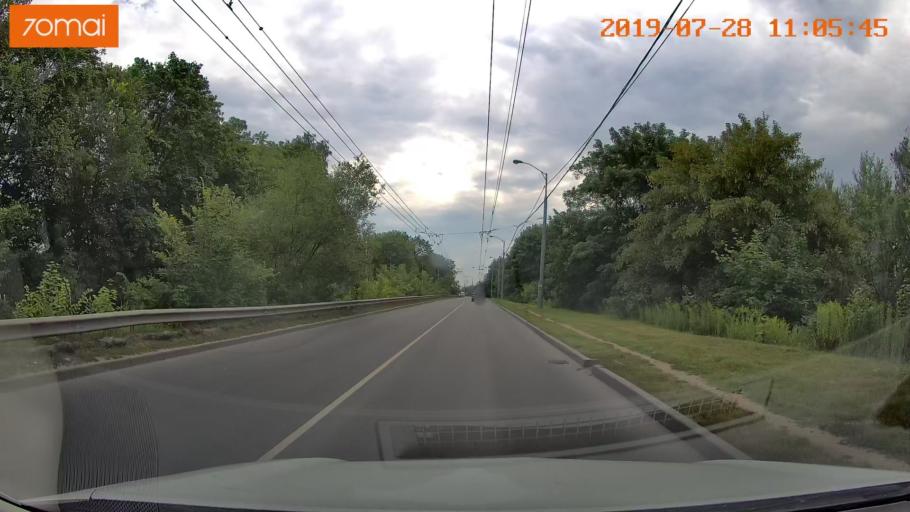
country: RU
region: Kaliningrad
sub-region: Gorod Kaliningrad
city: Kaliningrad
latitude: 54.7167
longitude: 20.3979
